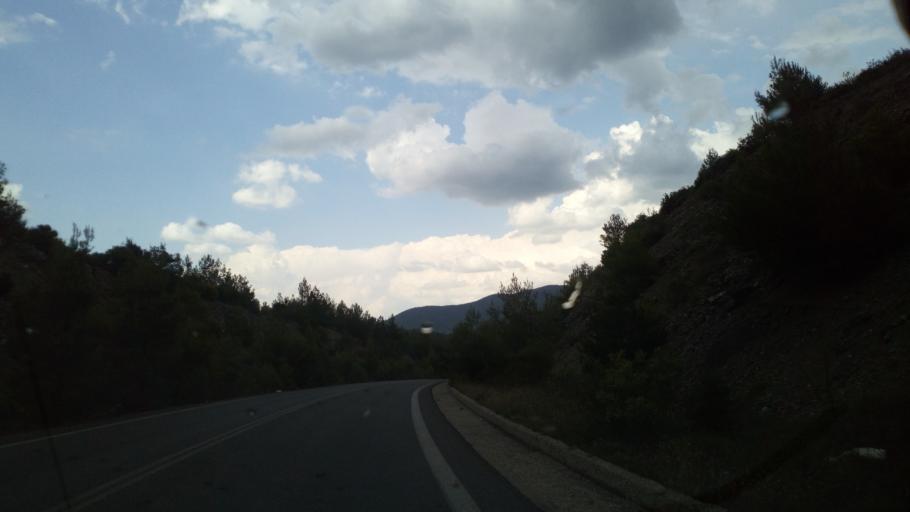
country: GR
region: Central Macedonia
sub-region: Nomos Chalkidikis
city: Polygyros
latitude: 40.3591
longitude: 23.4388
